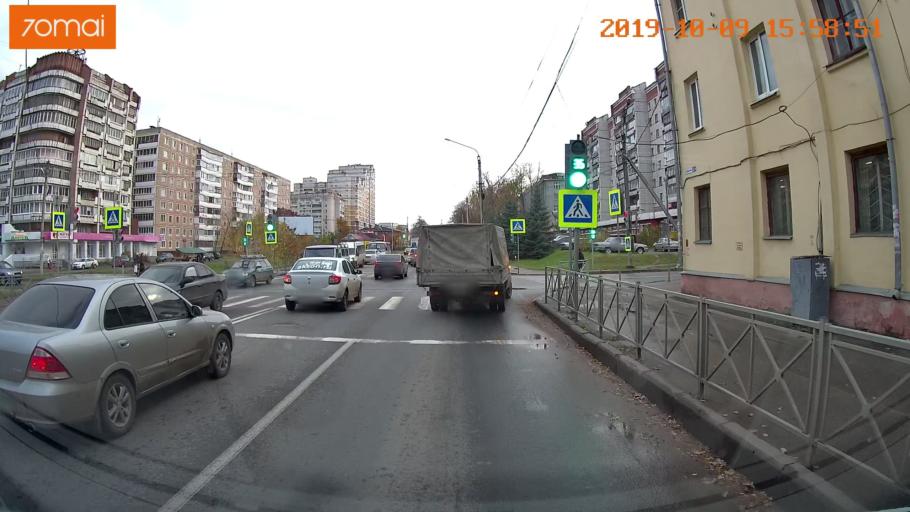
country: RU
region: Kostroma
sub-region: Kostromskoy Rayon
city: Kostroma
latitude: 57.7671
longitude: 40.9510
